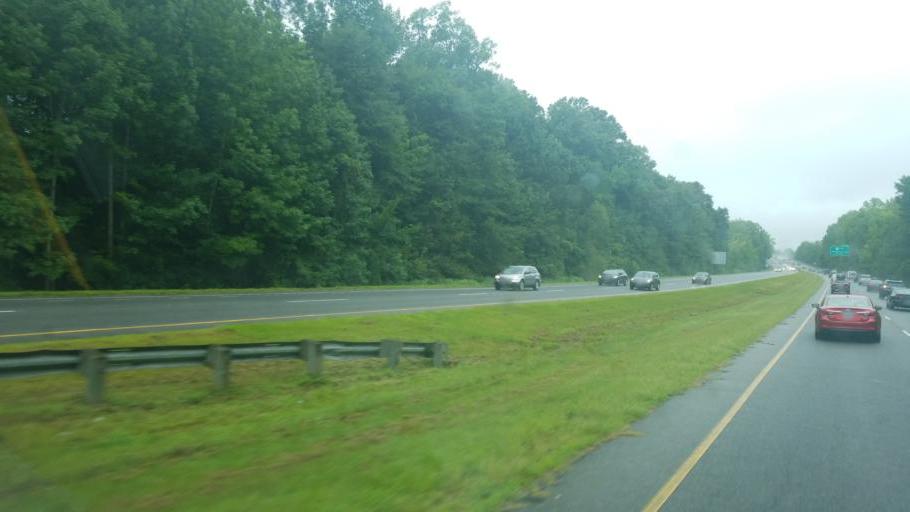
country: US
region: Virginia
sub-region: City of Chesapeake
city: Chesapeake
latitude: 36.7111
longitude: -76.2255
